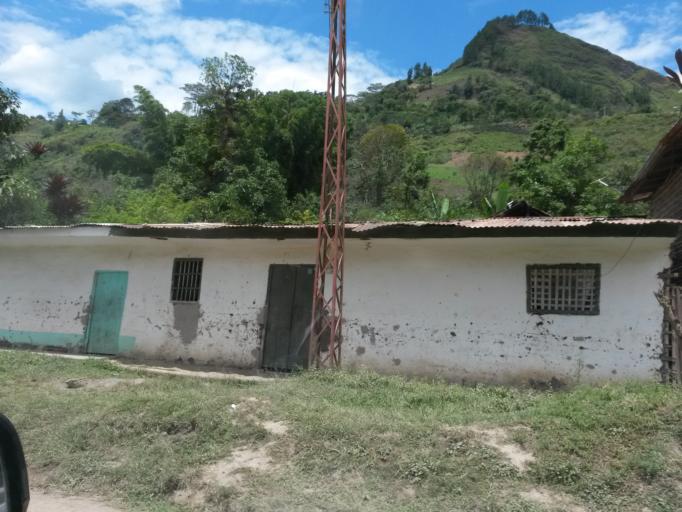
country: CO
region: Cauca
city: Inza
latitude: 2.5533
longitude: -76.0512
